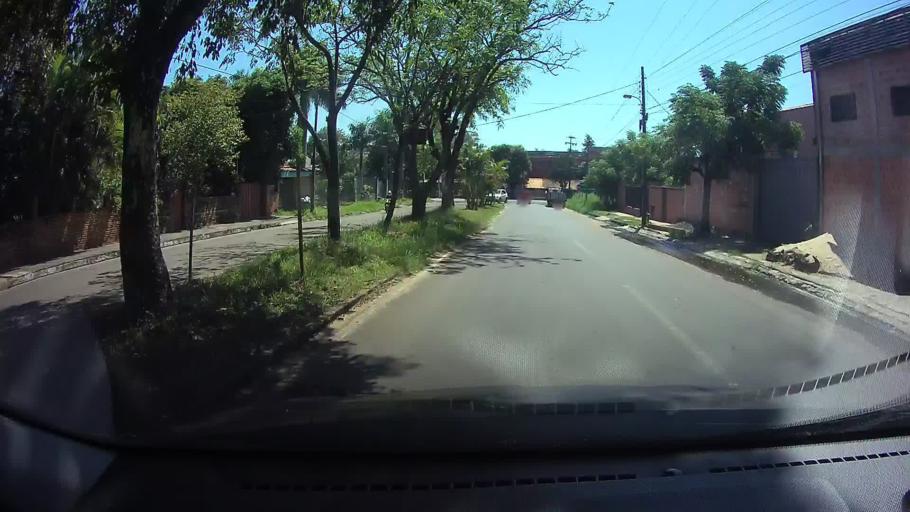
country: PY
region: Central
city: Fernando de la Mora
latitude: -25.2856
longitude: -57.5196
